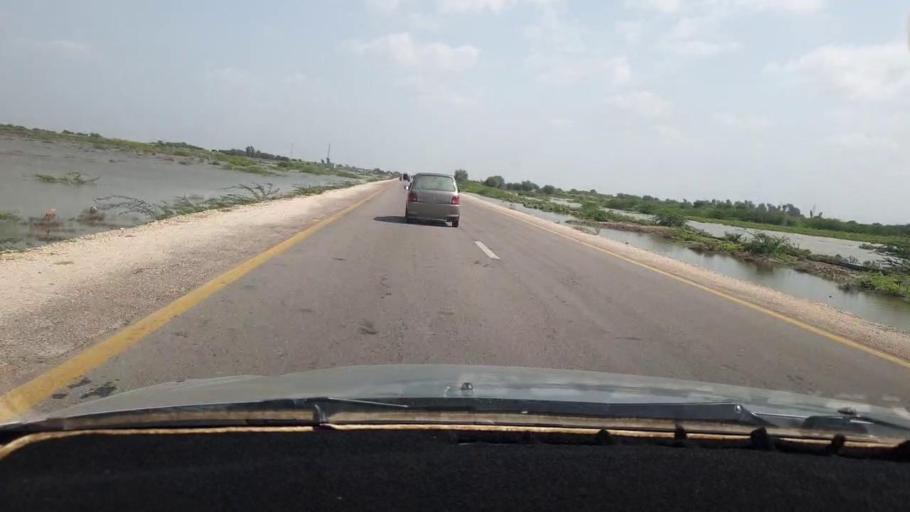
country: PK
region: Sindh
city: Digri
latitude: 25.1245
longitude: 69.1462
